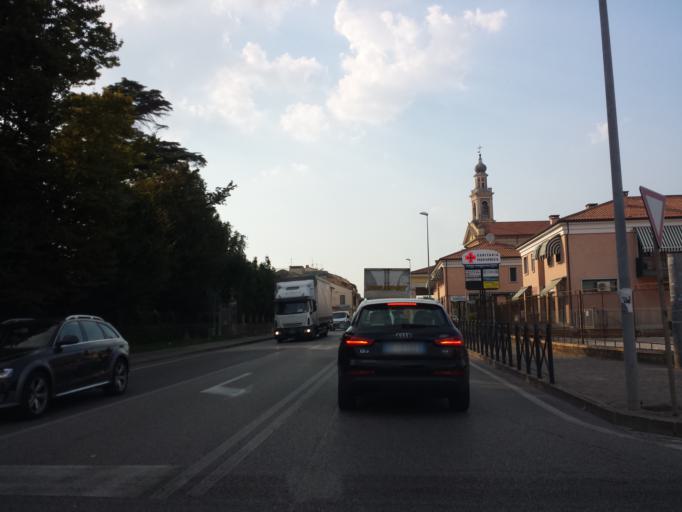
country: IT
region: Veneto
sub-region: Provincia di Padova
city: Mestrino
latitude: 45.4411
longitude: 11.7610
